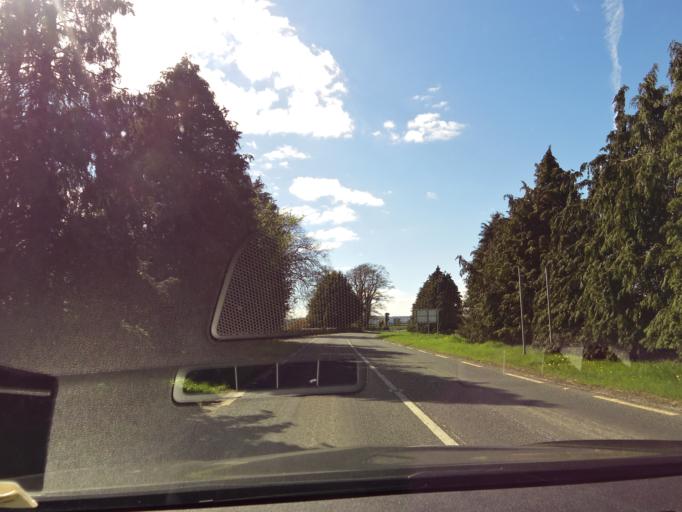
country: IE
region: Leinster
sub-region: Kildare
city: Athy
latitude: 52.9996
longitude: -7.0068
